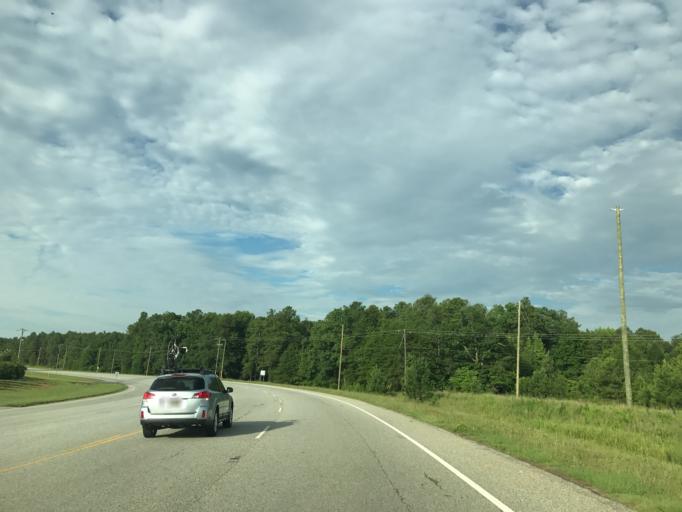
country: US
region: South Carolina
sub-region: Greenville County
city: Greer
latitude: 34.8972
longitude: -82.1963
